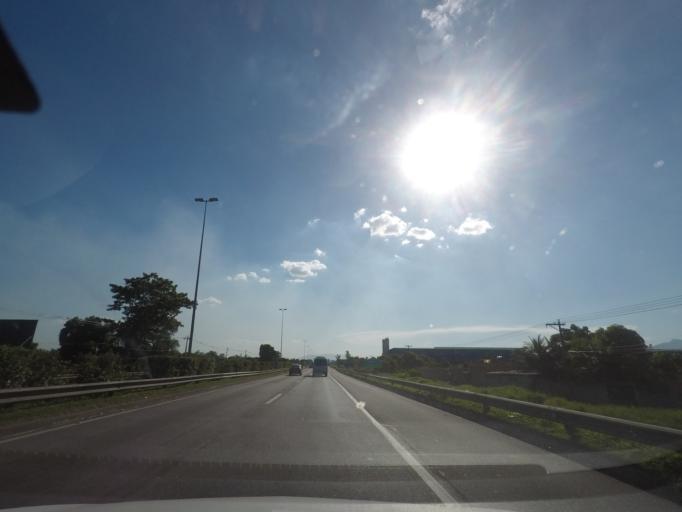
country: BR
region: Rio de Janeiro
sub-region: Duque De Caxias
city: Duque de Caxias
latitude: -22.6536
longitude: -43.2415
